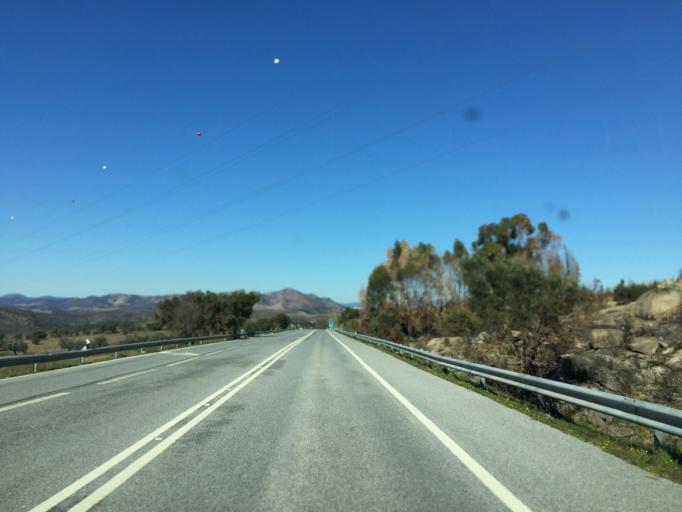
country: PT
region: Portalegre
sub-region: Nisa
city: Nisa
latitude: 39.5247
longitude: -7.7836
